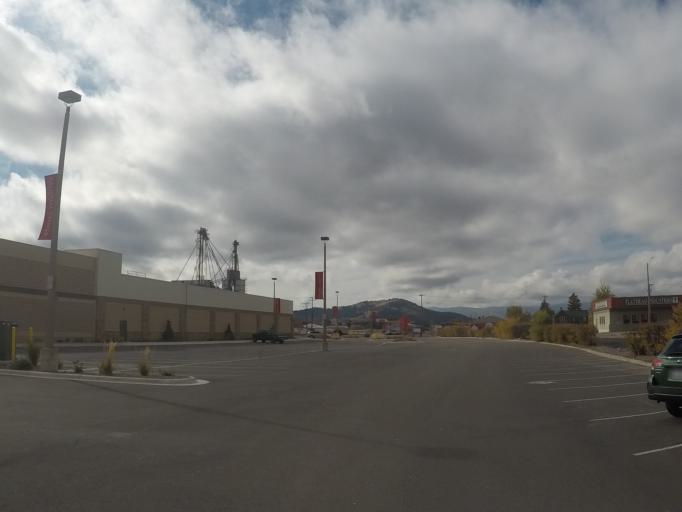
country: US
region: Montana
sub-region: Flathead County
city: Kalispell
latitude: 48.1995
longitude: -114.3184
